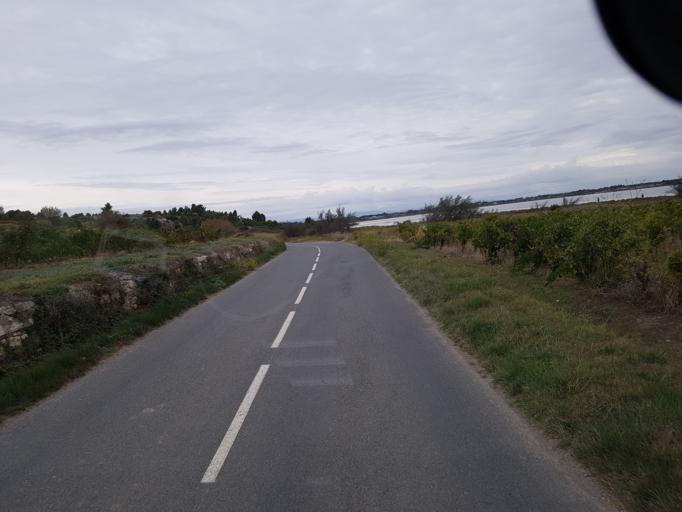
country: FR
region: Languedoc-Roussillon
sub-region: Departement de l'Aude
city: Peyriac-de-Mer
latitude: 43.1278
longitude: 2.9869
